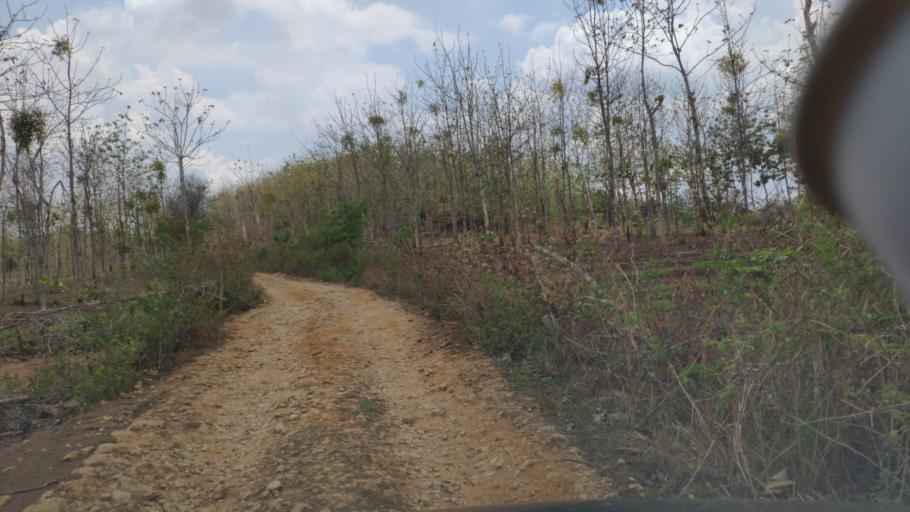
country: ID
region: Central Java
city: Ngapus
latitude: -6.9609
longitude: 111.2231
